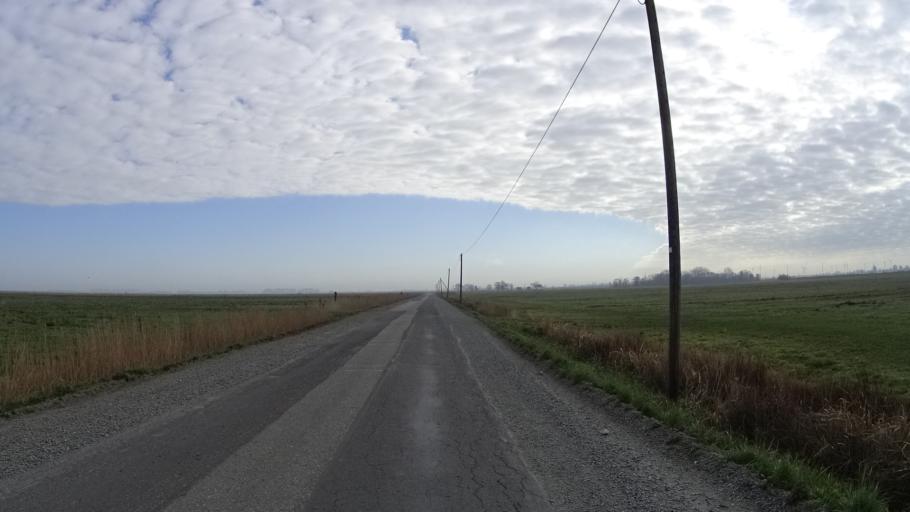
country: DE
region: Lower Saxony
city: Emden
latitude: 53.4043
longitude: 7.3130
